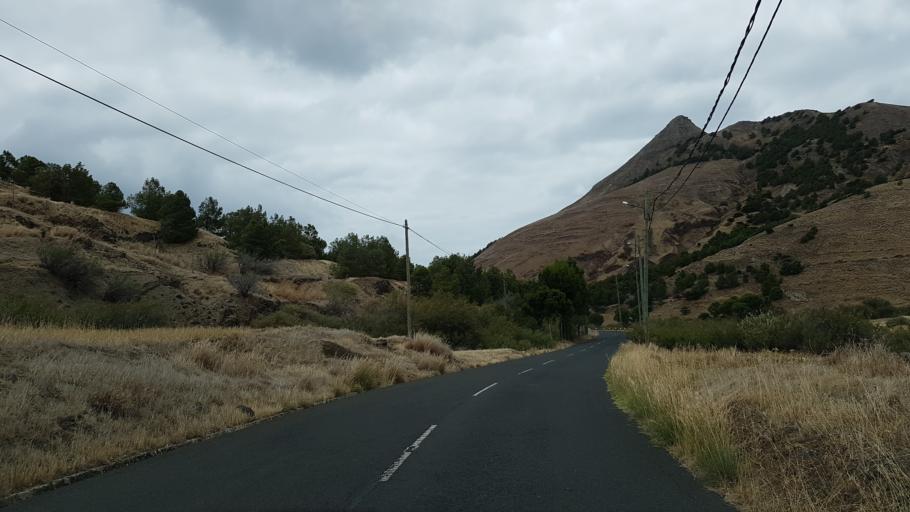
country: PT
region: Madeira
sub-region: Porto Santo
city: Vila de Porto Santo
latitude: 33.0734
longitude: -16.3091
